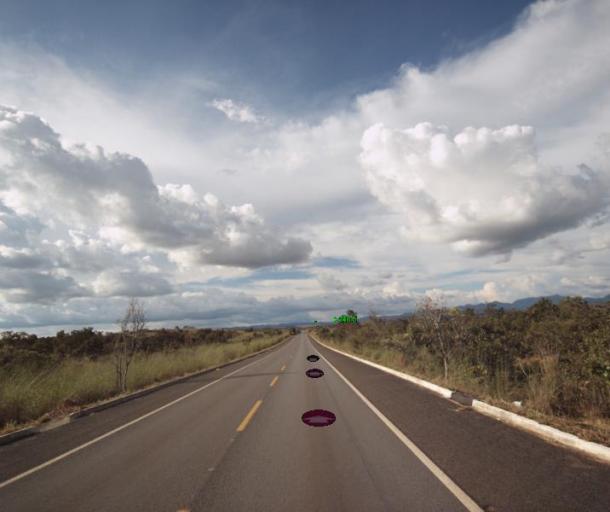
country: BR
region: Goias
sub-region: Barro Alto
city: Barro Alto
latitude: -14.8144
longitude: -48.6365
